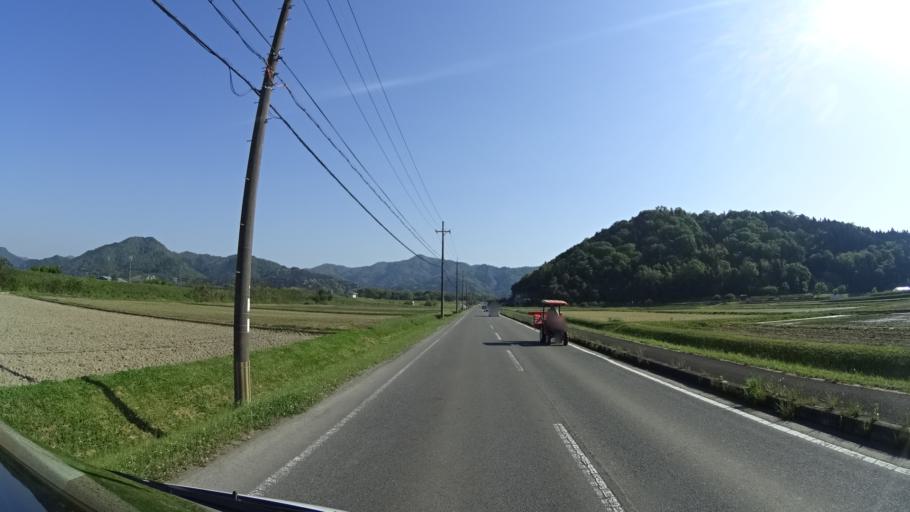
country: JP
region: Kyoto
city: Ayabe
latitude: 35.3160
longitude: 135.2094
